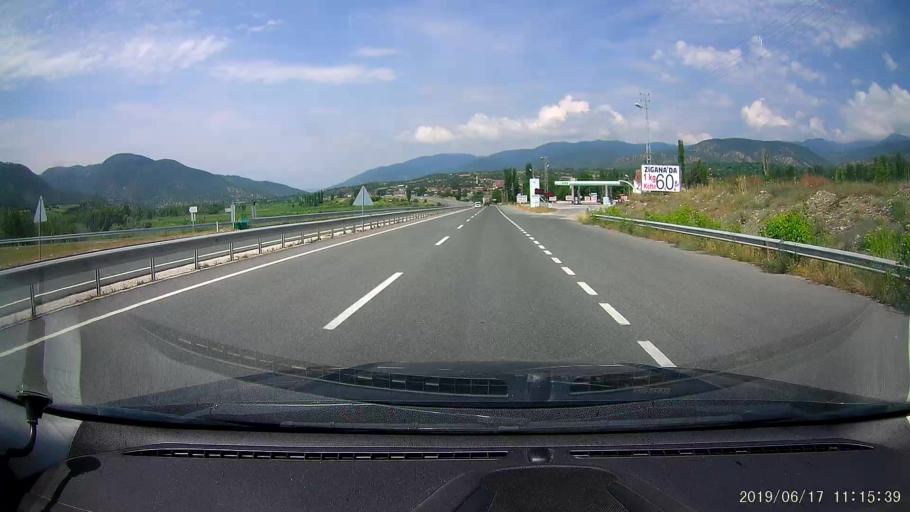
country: TR
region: Kastamonu
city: Tosya
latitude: 40.9508
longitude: 33.9190
